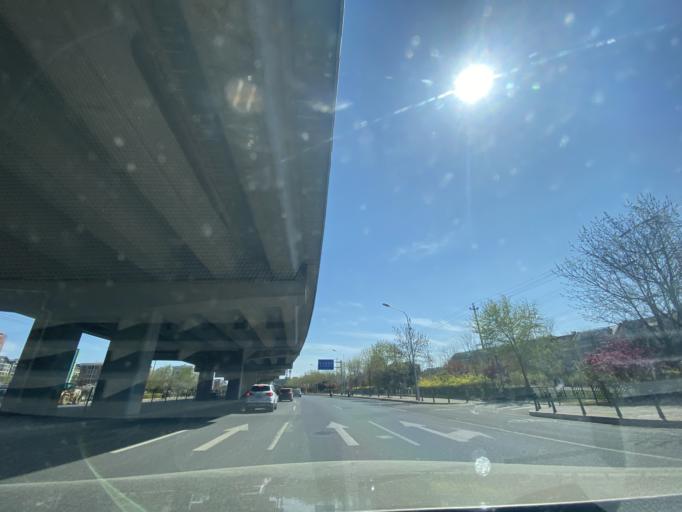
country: CN
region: Beijing
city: Babaoshan
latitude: 39.9230
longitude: 116.2513
